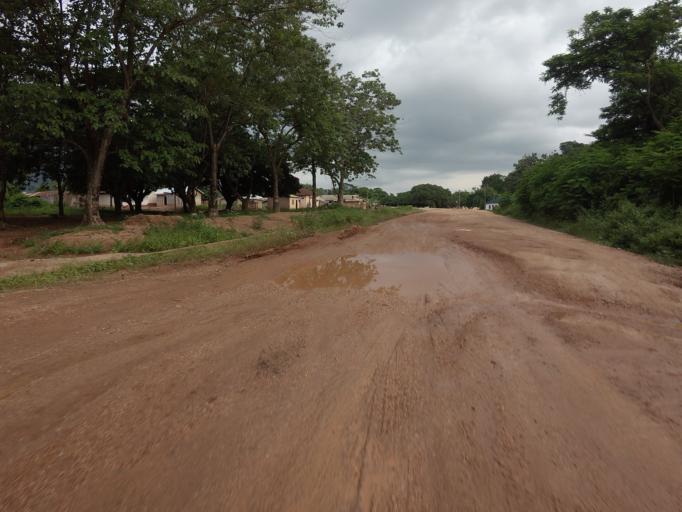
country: GH
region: Volta
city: Kpandu
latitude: 6.8166
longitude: 0.3734
